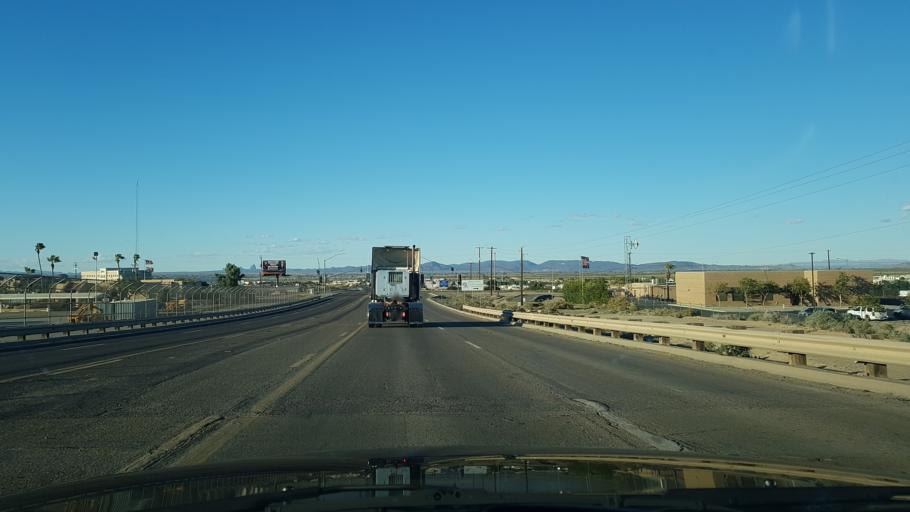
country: US
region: Arizona
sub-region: Yuma County
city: Yuma
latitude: 32.6892
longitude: -114.5988
